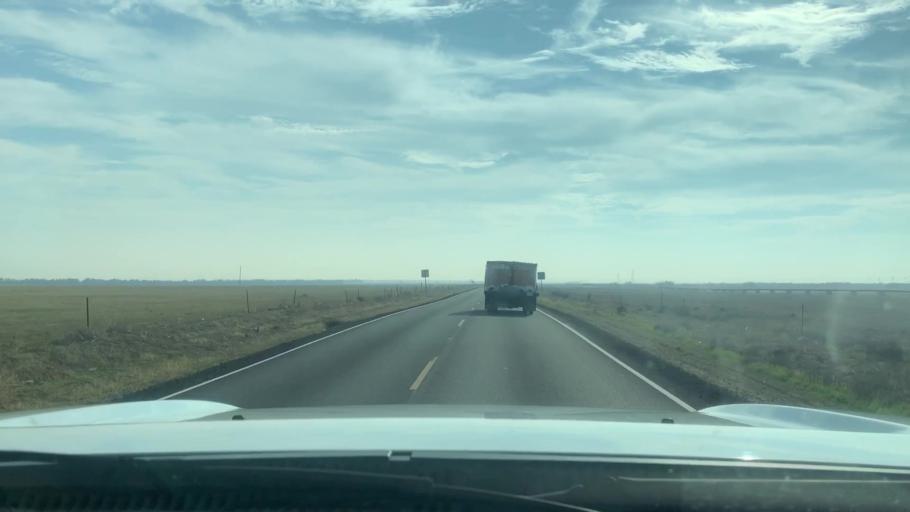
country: US
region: California
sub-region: Kern County
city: Lost Hills
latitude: 35.5555
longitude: -119.7945
